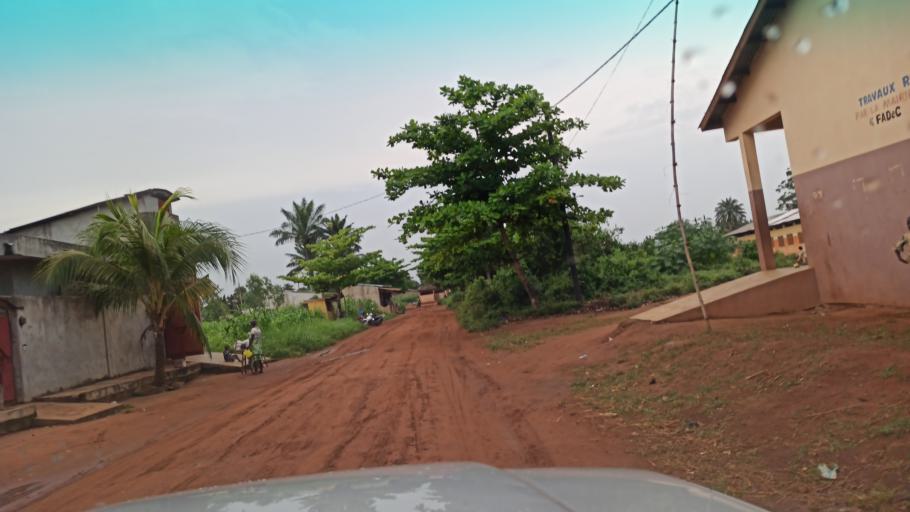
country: BJ
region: Queme
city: Porto-Novo
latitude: 6.4773
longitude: 2.6746
